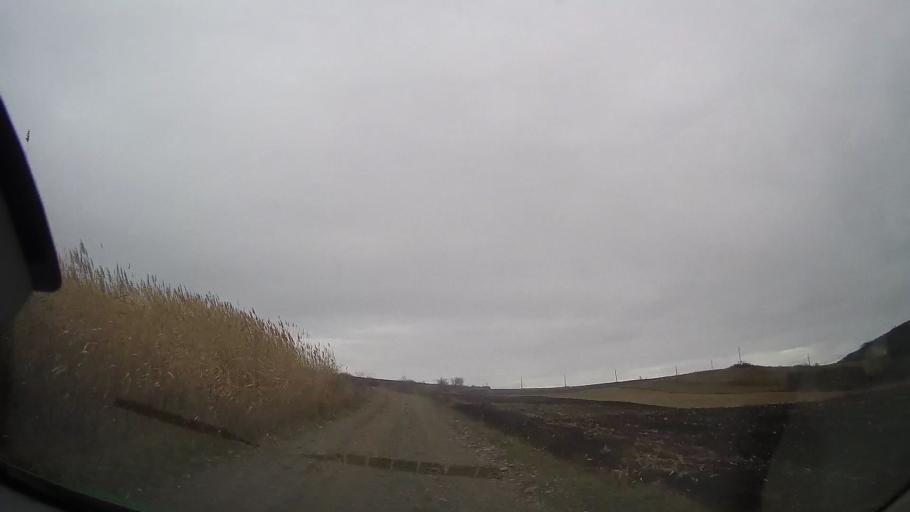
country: RO
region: Mures
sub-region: Comuna Bala
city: Bala
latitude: 46.6974
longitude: 24.4908
